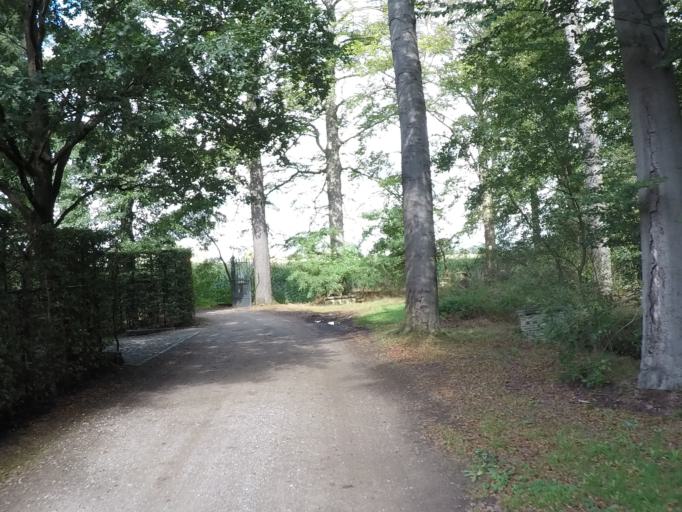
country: BE
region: Flanders
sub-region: Provincie Antwerpen
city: Vorselaar
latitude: 51.2151
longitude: 4.7809
